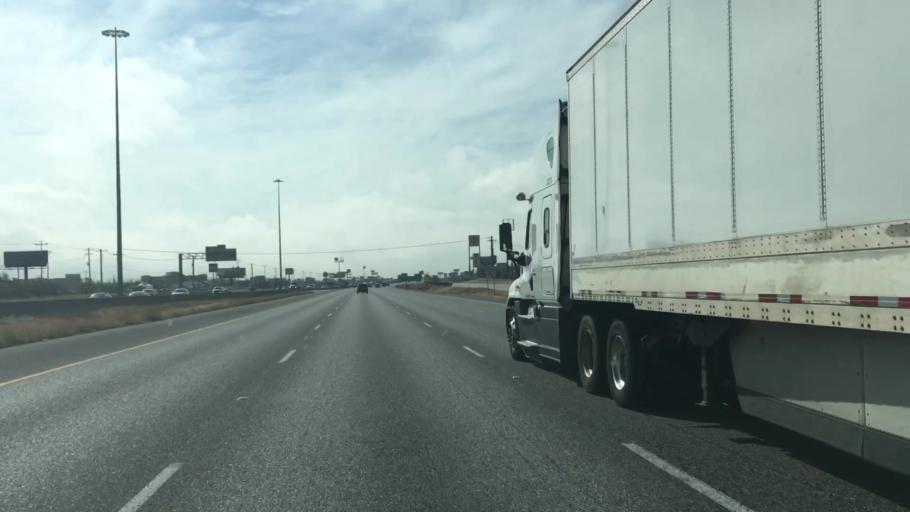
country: US
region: Texas
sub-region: Hays County
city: Buda
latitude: 30.0978
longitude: -97.8140
